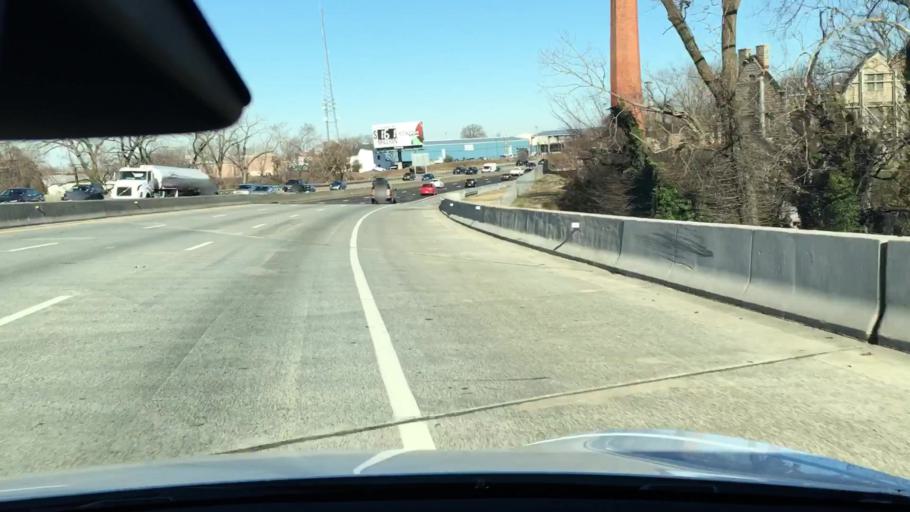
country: US
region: Virginia
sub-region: City of Richmond
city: Richmond
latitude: 37.5597
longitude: -77.4531
